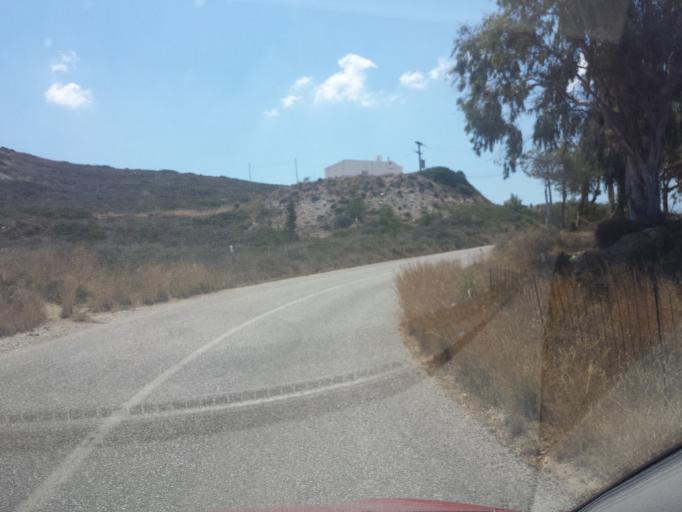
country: GR
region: South Aegean
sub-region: Nomos Kykladon
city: Adamas
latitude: 36.6867
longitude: 24.5011
